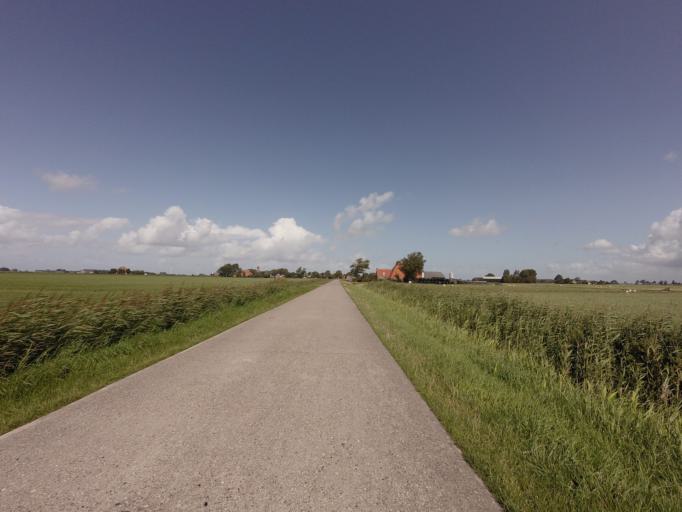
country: NL
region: Friesland
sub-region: Sudwest Fryslan
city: Makkum
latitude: 53.0747
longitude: 5.4532
